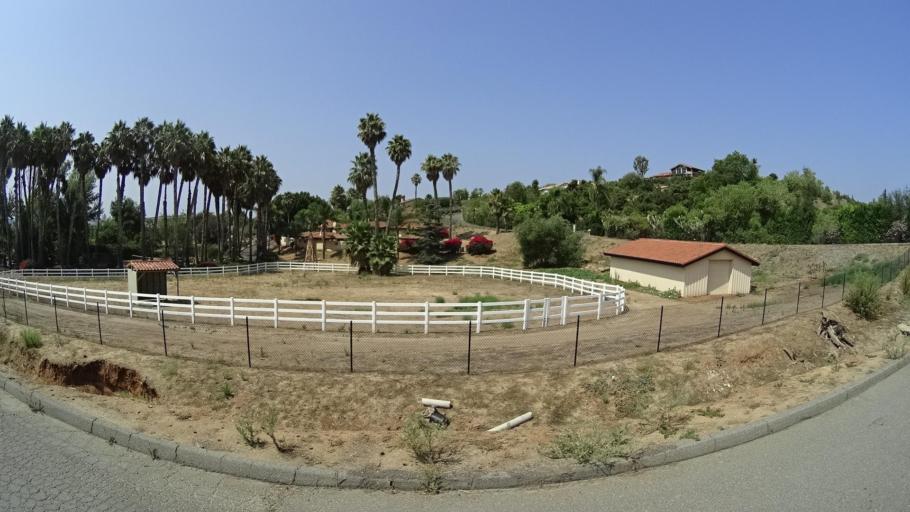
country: US
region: California
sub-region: San Diego County
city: Bonsall
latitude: 33.2759
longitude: -117.2450
